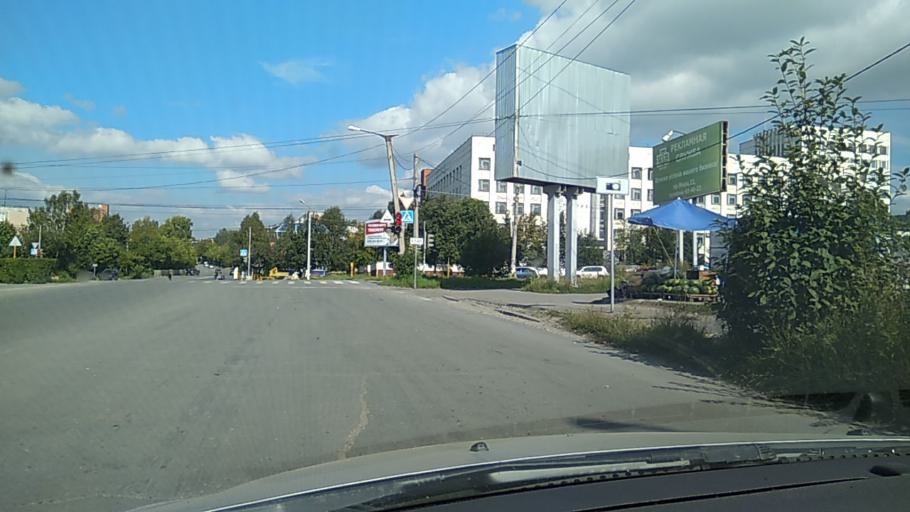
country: RU
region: Chelyabinsk
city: Zlatoust
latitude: 55.1130
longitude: 59.7062
